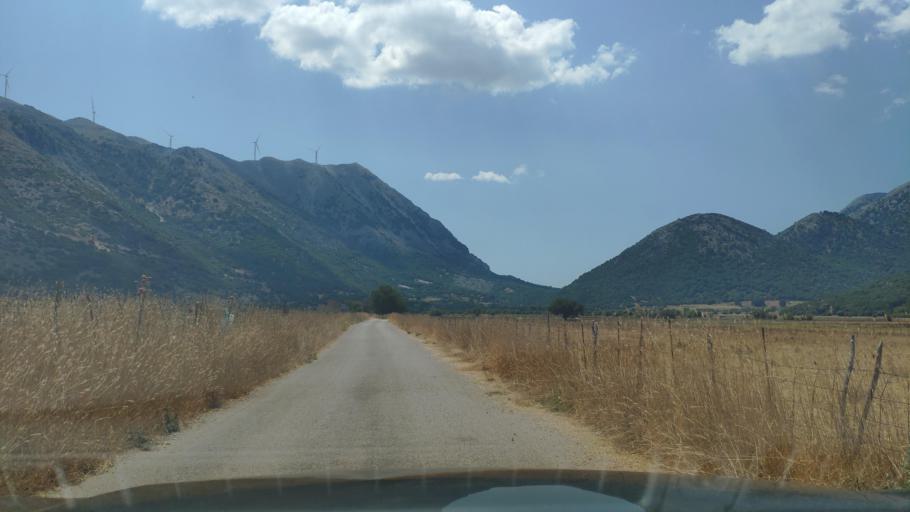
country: GR
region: West Greece
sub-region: Nomos Aitolias kai Akarnanias
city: Monastirakion
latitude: 38.7870
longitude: 20.9657
